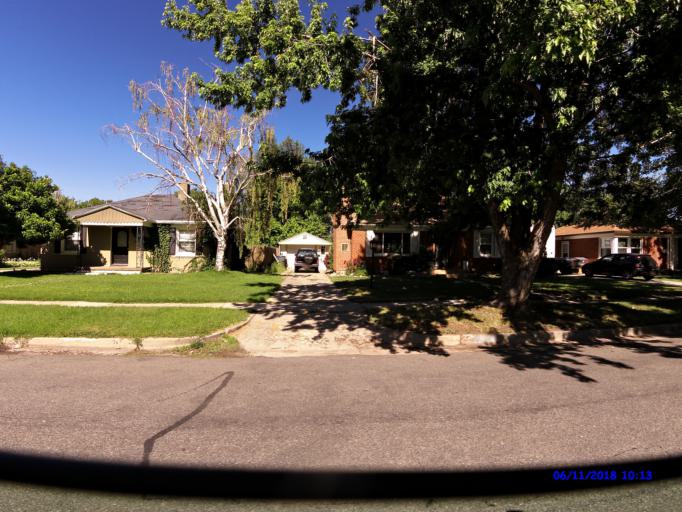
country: US
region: Utah
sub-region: Weber County
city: South Ogden
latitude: 41.2089
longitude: -111.9473
